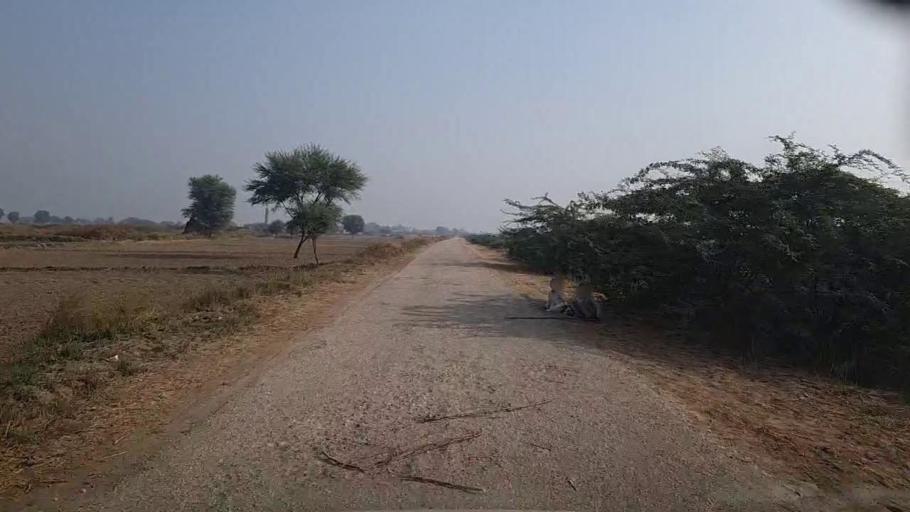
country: PK
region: Sindh
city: Setharja Old
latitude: 27.0644
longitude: 68.4536
